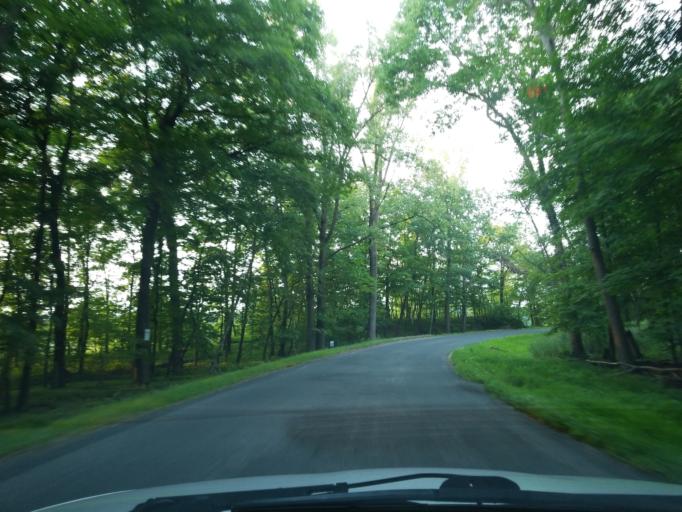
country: US
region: Minnesota
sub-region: Washington County
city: Stillwater
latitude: 45.0871
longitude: -92.7713
